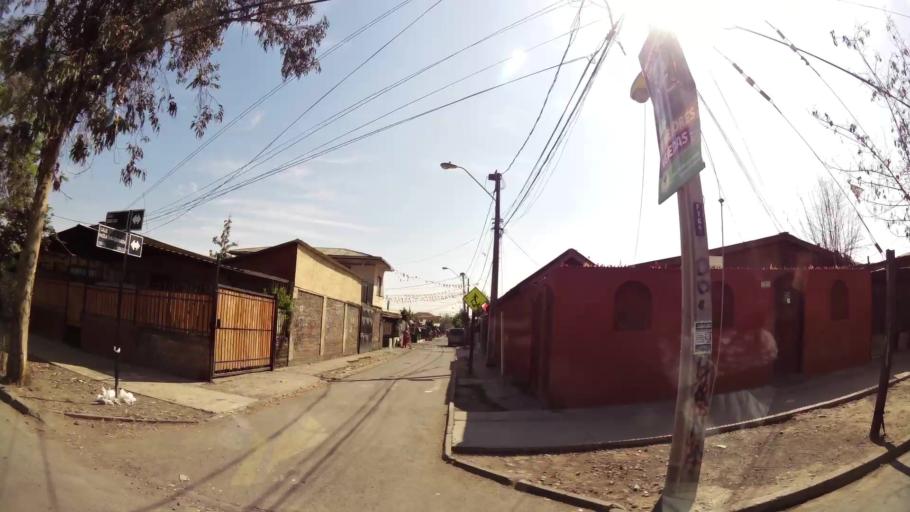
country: CL
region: Santiago Metropolitan
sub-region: Provincia de Santiago
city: La Pintana
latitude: -33.5594
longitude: -70.6610
